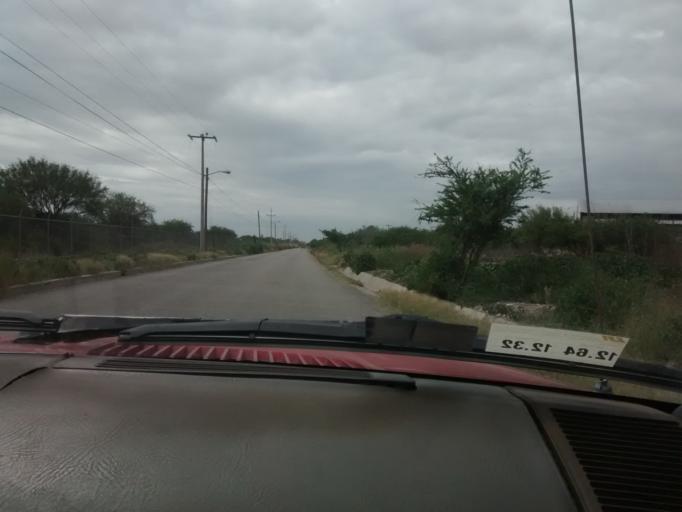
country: MX
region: Puebla
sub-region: Santiago Miahuatlan
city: San Jose Monte Chiquito
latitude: 18.4986
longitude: -97.4238
